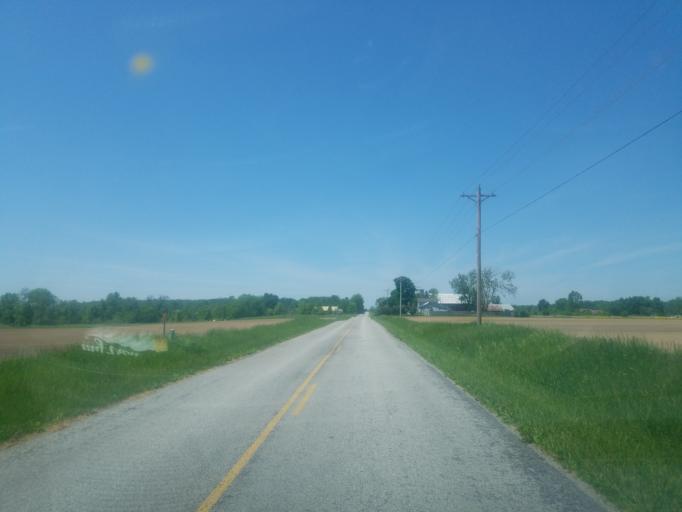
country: US
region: Ohio
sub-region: Huron County
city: New London
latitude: 41.1160
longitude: -82.3715
